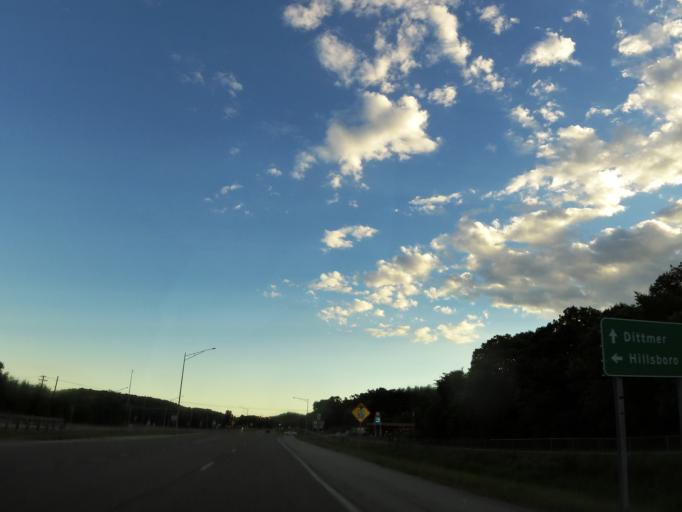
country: US
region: Missouri
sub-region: Jefferson County
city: Cedar Hill
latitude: 38.3429
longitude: -90.6526
